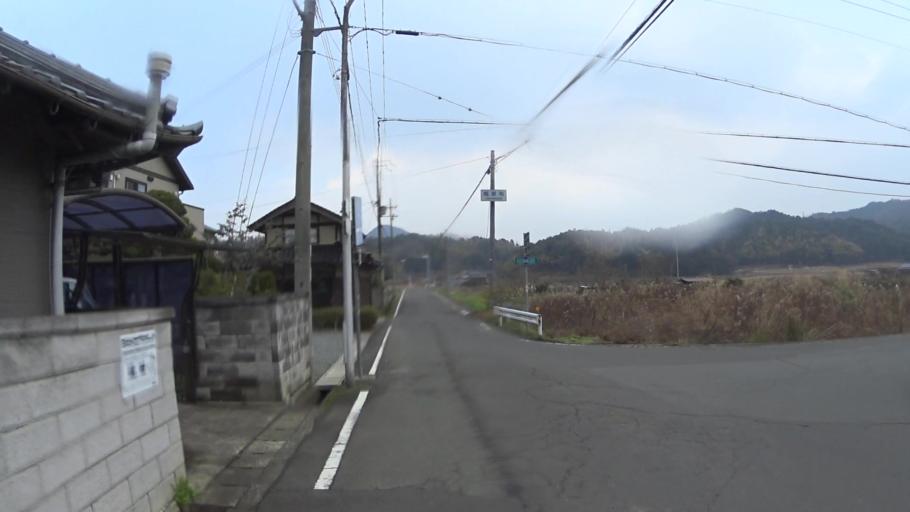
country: JP
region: Kyoto
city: Maizuru
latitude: 35.4300
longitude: 135.2959
